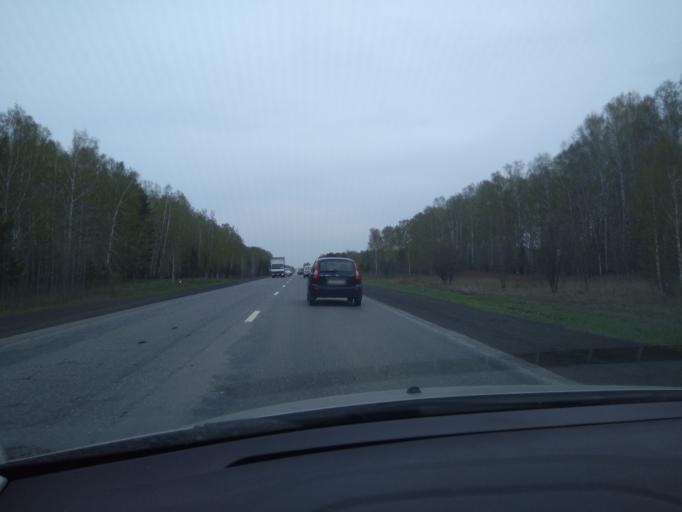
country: RU
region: Sverdlovsk
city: Gryaznovskoye
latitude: 56.7788
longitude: 61.5803
